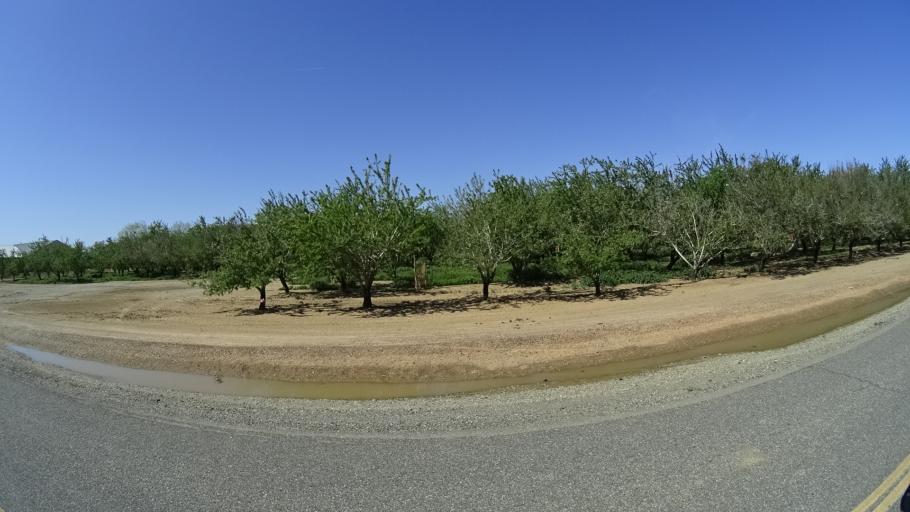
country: US
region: California
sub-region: Glenn County
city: Hamilton City
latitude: 39.7867
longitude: -122.0524
